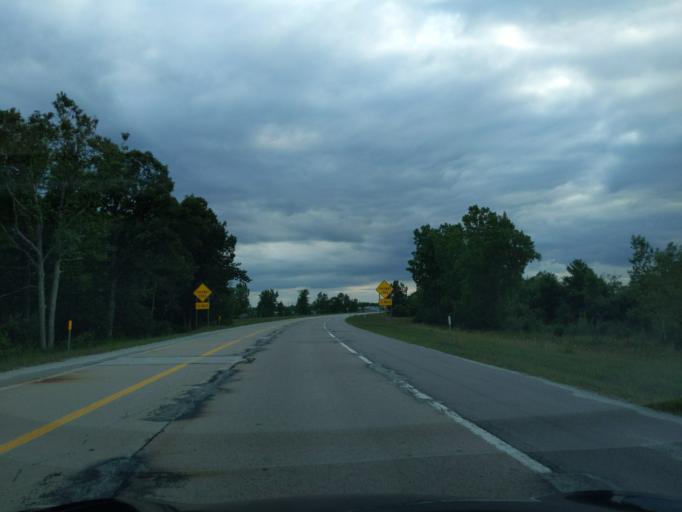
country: US
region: Michigan
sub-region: Isabella County
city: Mount Pleasant
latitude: 43.6206
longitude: -84.7616
